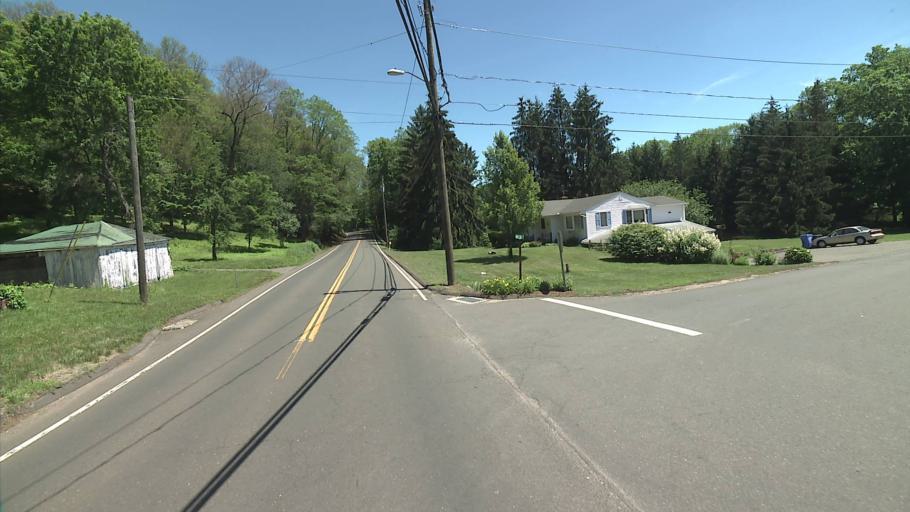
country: US
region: Connecticut
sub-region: New Haven County
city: North Branford
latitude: 41.3705
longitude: -72.7174
